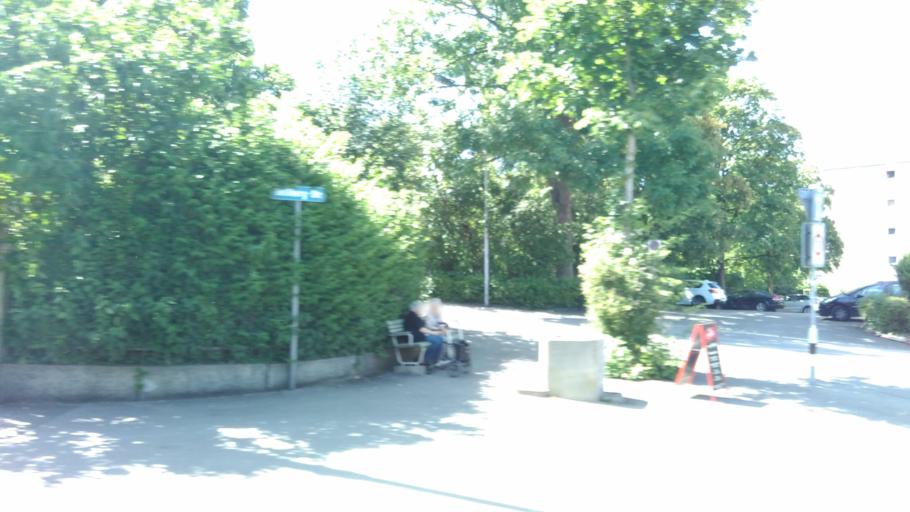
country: CH
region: Zurich
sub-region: Bezirk Zuerich
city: Zuerich (Kreis 3) / Alt-Wiedikon
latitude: 47.3579
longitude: 8.5144
